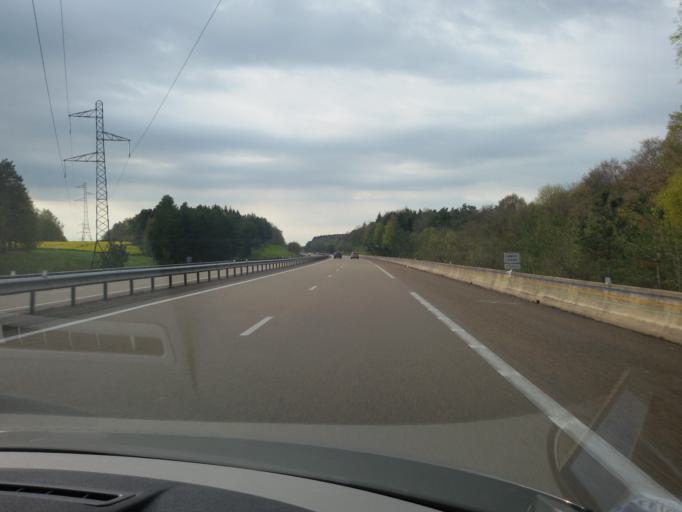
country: FR
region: Champagne-Ardenne
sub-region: Departement de la Haute-Marne
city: Chamarandes-Choignes
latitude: 47.9977
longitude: 5.1204
